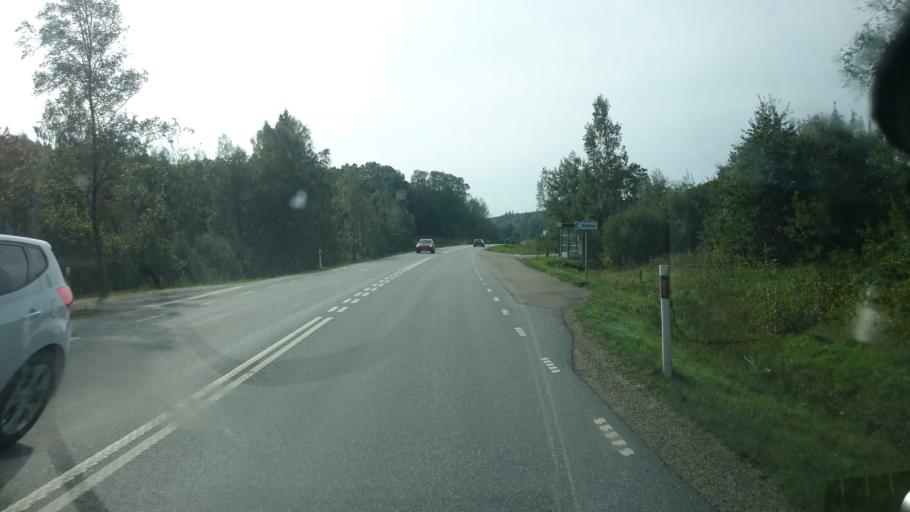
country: SE
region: Vaestra Goetaland
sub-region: Alingsas Kommun
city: Sollebrunn
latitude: 58.0487
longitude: 12.4686
